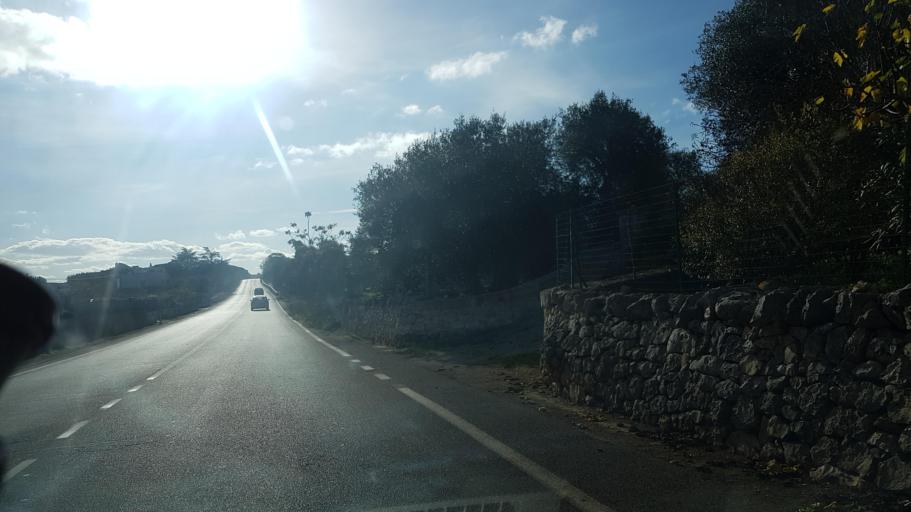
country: IT
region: Apulia
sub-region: Provincia di Brindisi
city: Ceglie Messapica
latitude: 40.6597
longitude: 17.5302
